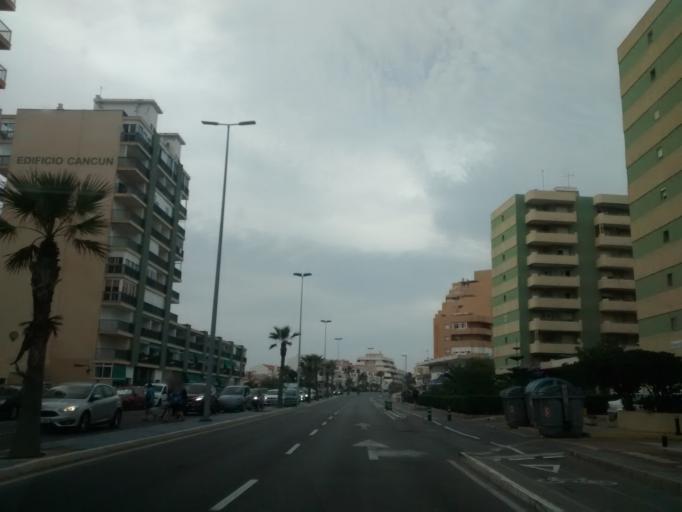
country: ES
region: Murcia
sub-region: Murcia
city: La Manga del Mar Menor
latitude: 37.6883
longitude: -0.7370
